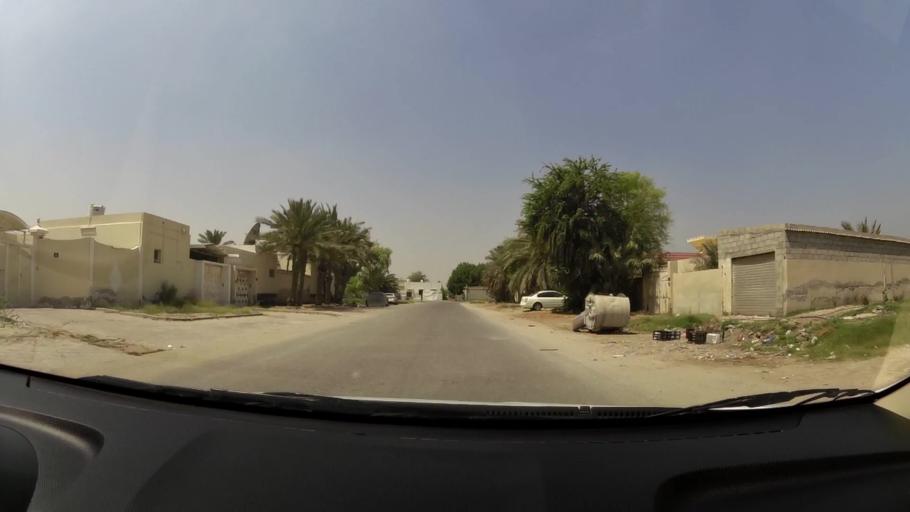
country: AE
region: Umm al Qaywayn
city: Umm al Qaywayn
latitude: 25.5623
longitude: 55.5563
